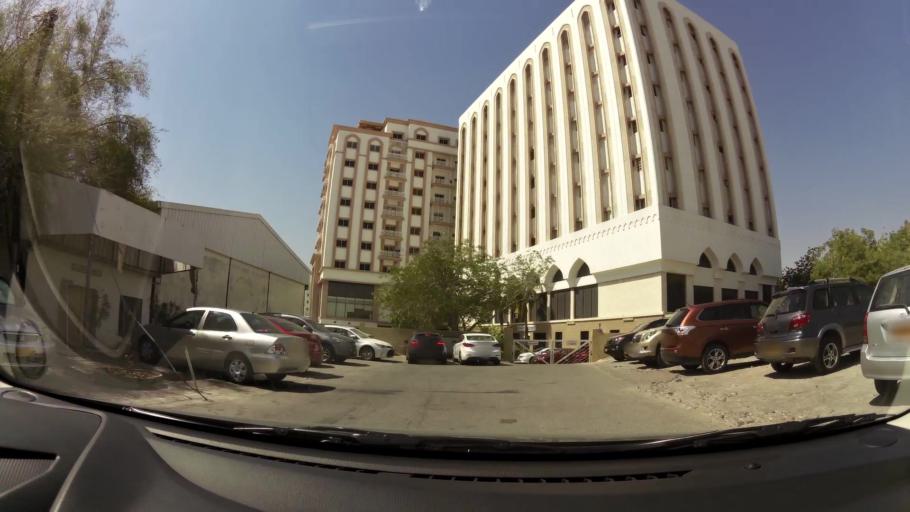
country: OM
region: Muhafazat Masqat
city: Muscat
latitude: 23.6007
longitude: 58.5382
